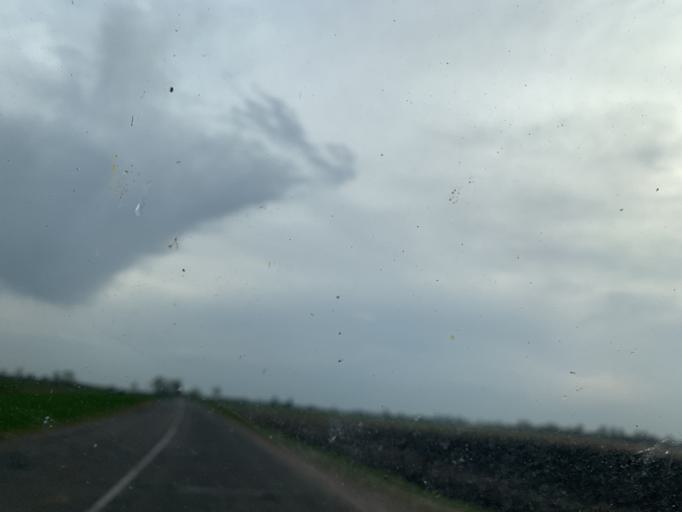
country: BY
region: Minsk
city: Kapyl'
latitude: 53.3003
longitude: 27.0415
